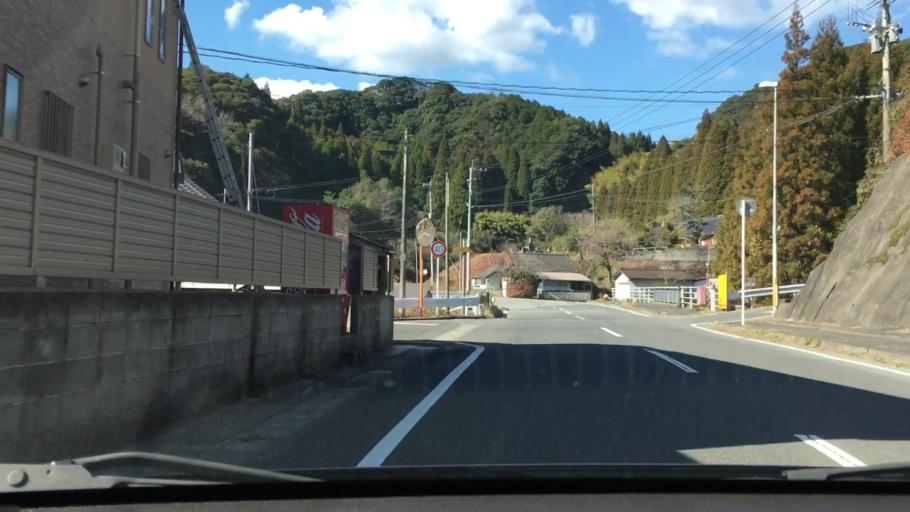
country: JP
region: Kagoshima
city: Ijuin
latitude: 31.6998
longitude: 130.4577
